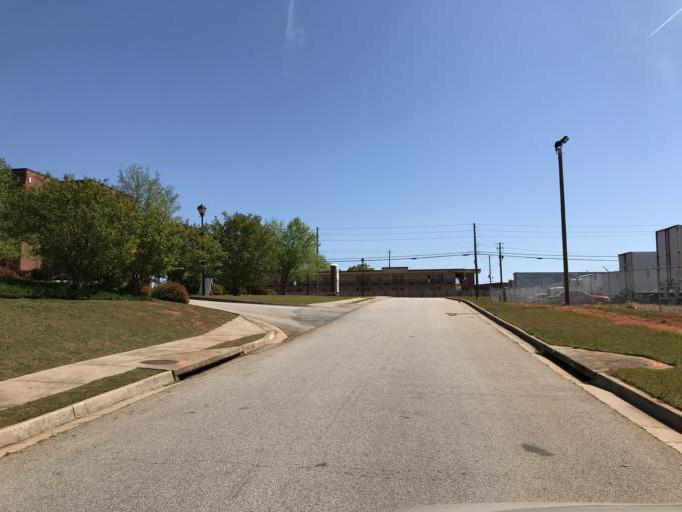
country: US
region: Georgia
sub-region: Henry County
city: McDonough
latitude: 33.4153
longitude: -84.1579
